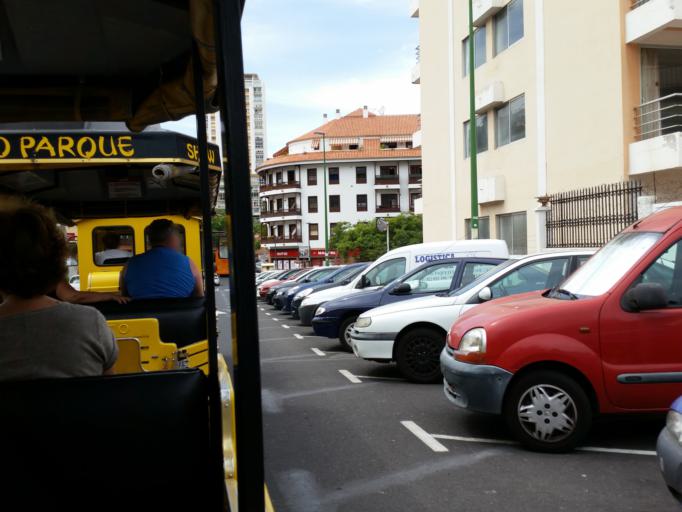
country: ES
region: Canary Islands
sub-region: Provincia de Santa Cruz de Tenerife
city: Puerto de la Cruz
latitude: 28.4154
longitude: -16.5444
